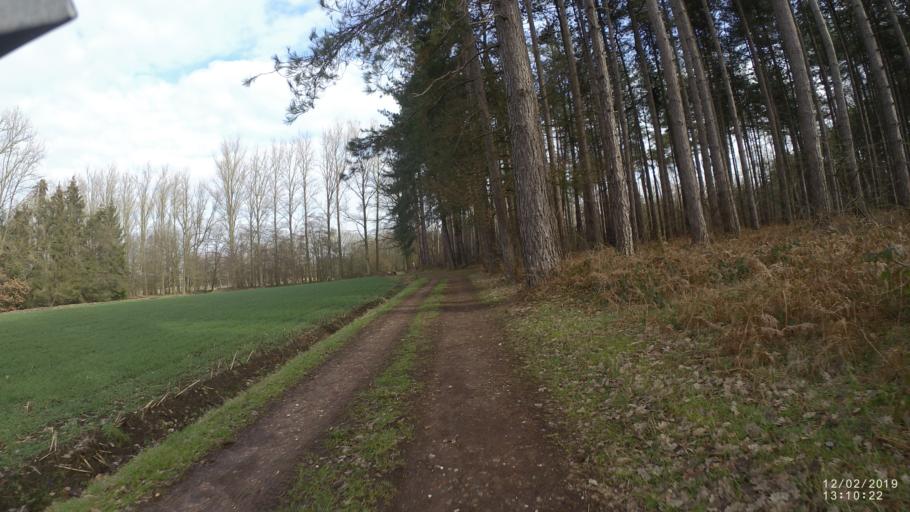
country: BE
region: Flanders
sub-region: Provincie Vlaams-Brabant
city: Scherpenheuvel-Zichem
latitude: 51.0063
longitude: 4.9231
